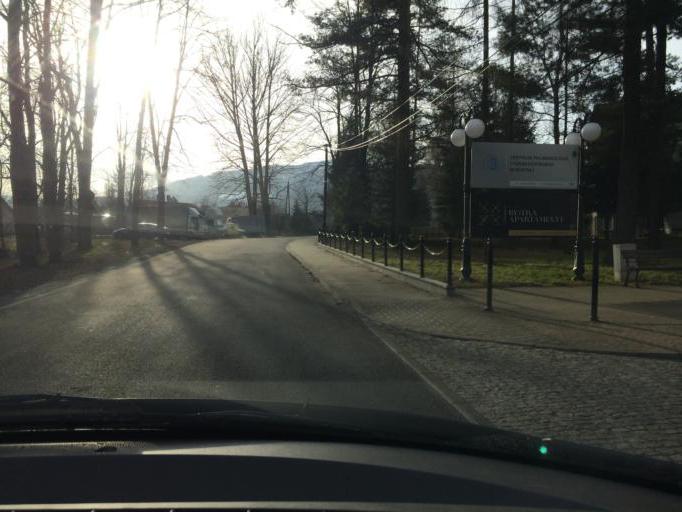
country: PL
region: Silesian Voivodeship
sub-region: Powiat bielski
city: Bystra
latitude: 49.7636
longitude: 19.0701
